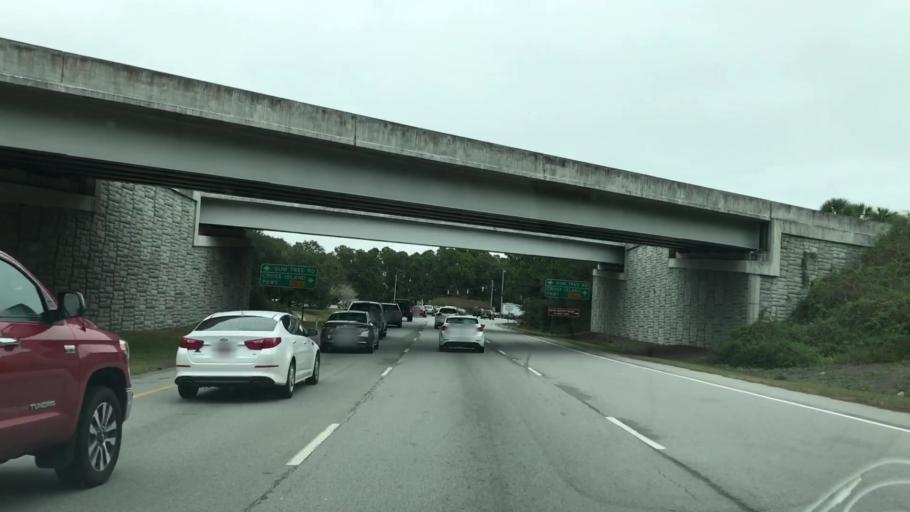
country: US
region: South Carolina
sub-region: Beaufort County
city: Hilton Head Island
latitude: 32.2153
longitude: -80.7404
